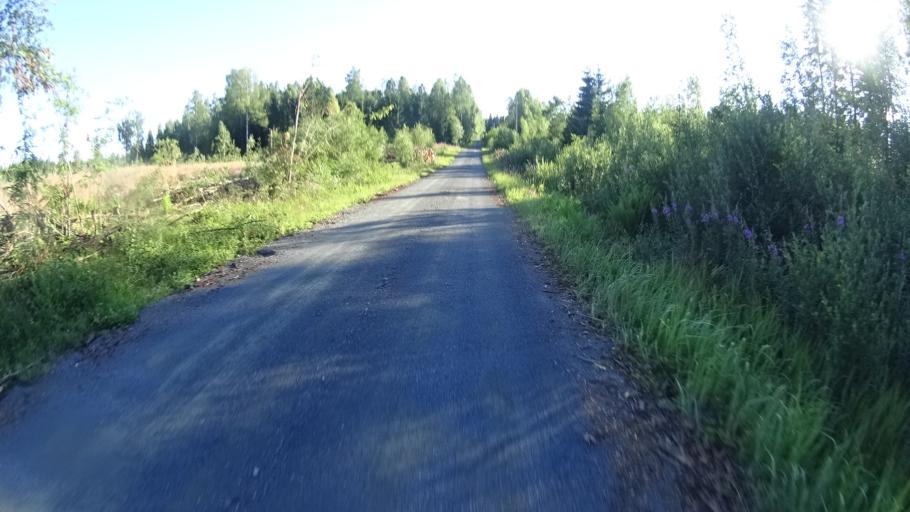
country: FI
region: Uusimaa
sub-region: Helsinki
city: Karkkila
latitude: 60.6455
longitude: 24.1227
